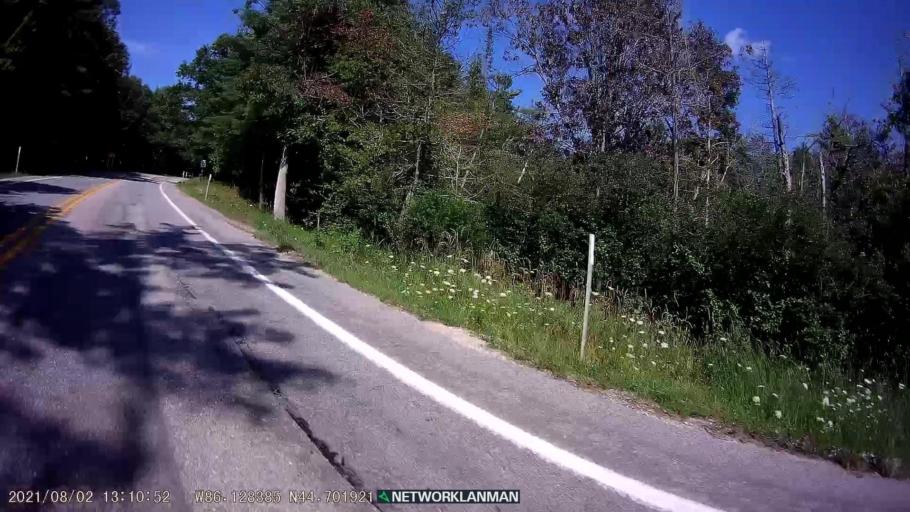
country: US
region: Michigan
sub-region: Benzie County
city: Beulah
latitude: 44.7021
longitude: -86.1283
